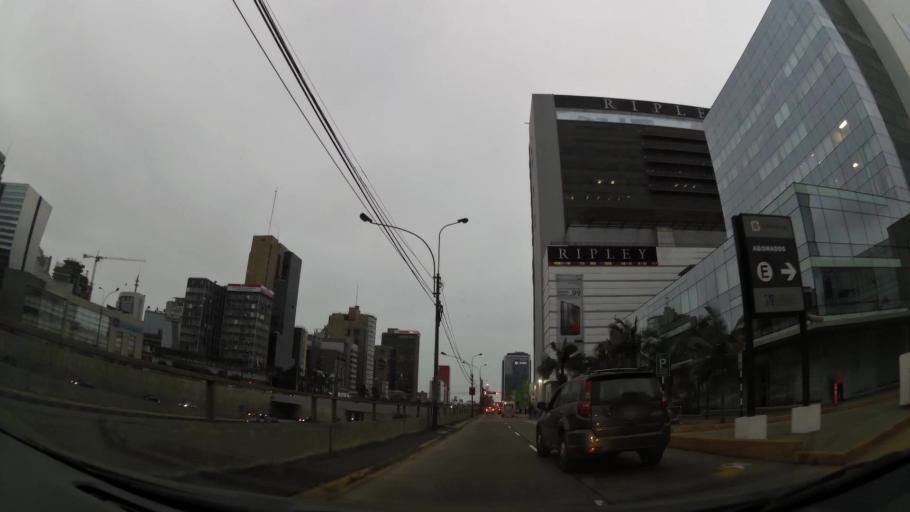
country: PE
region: Lima
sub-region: Lima
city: San Luis
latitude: -12.0936
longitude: -77.0239
